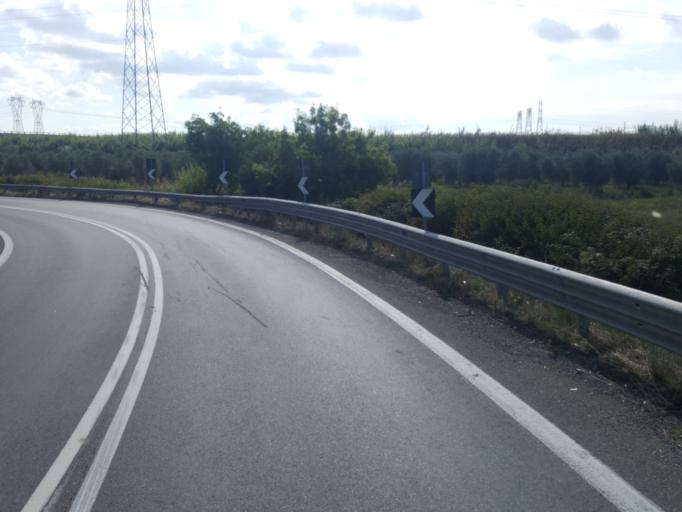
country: IT
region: Tuscany
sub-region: Provincia di Livorno
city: Venturina
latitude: 43.0121
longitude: 10.5969
